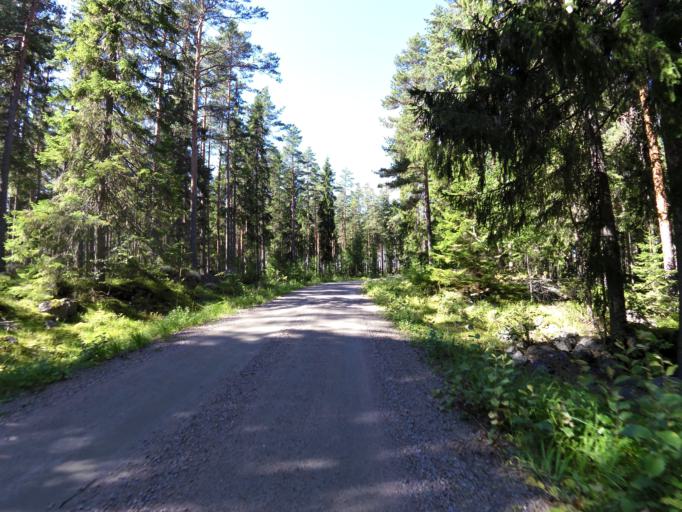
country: SE
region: Gaevleborg
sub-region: Ockelbo Kommun
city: Ockelbo
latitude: 60.7952
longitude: 16.8790
